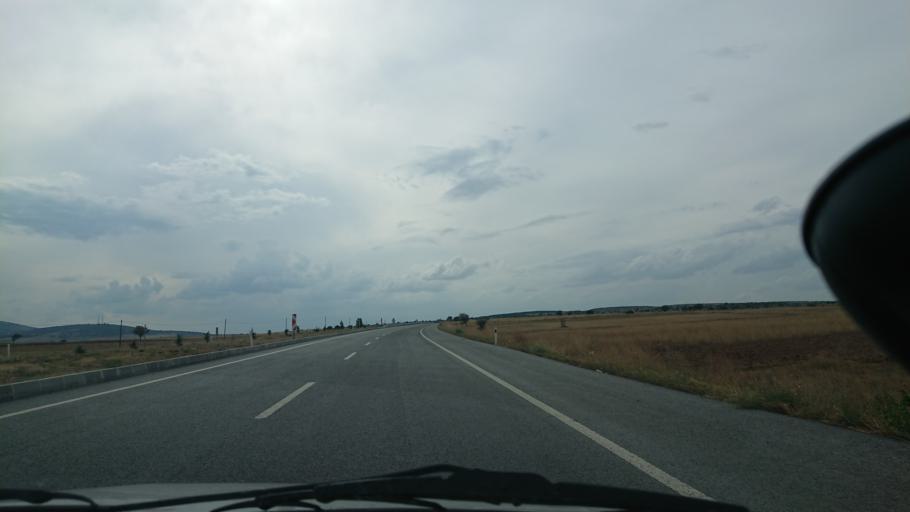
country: TR
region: Kuetahya
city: Aslanapa
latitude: 39.2490
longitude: 29.8245
